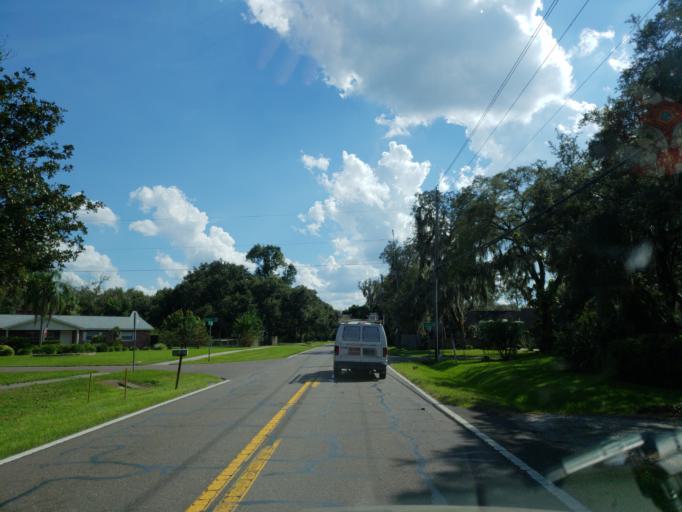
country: US
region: Florida
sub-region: Hillsborough County
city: Valrico
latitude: 27.9225
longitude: -82.2528
